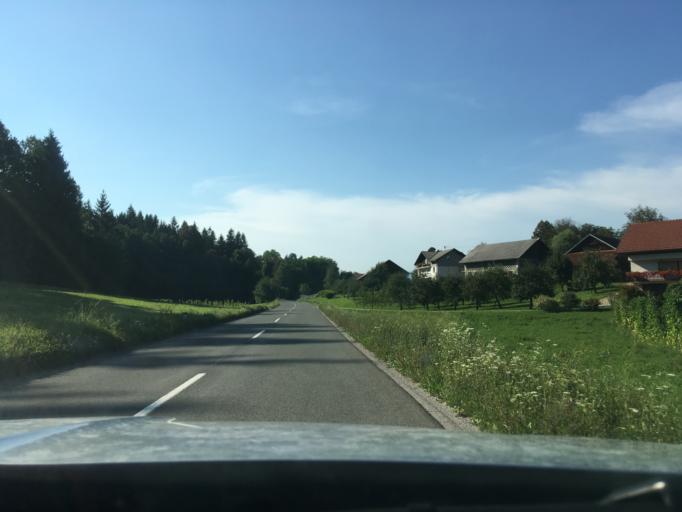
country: SI
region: Crnomelj
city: Crnomelj
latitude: 45.5067
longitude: 15.1885
